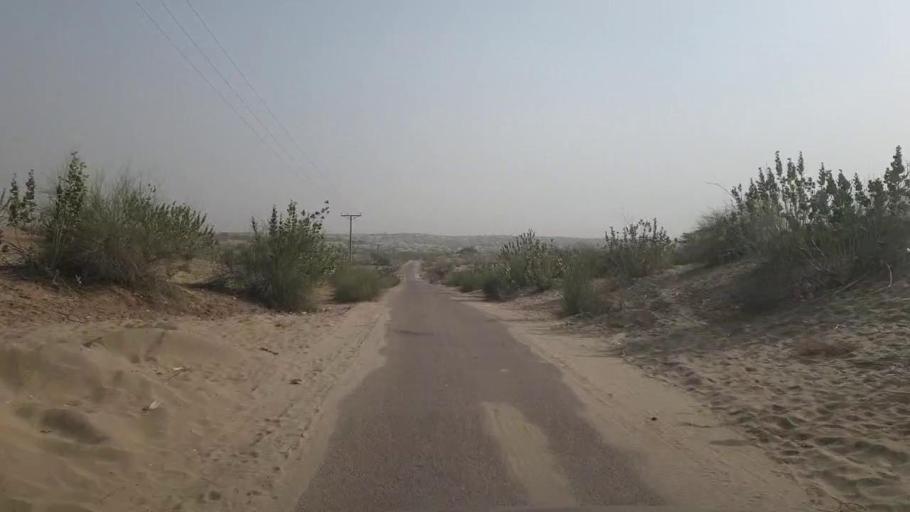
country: PK
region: Sindh
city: Chor
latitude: 25.5459
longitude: 69.9595
